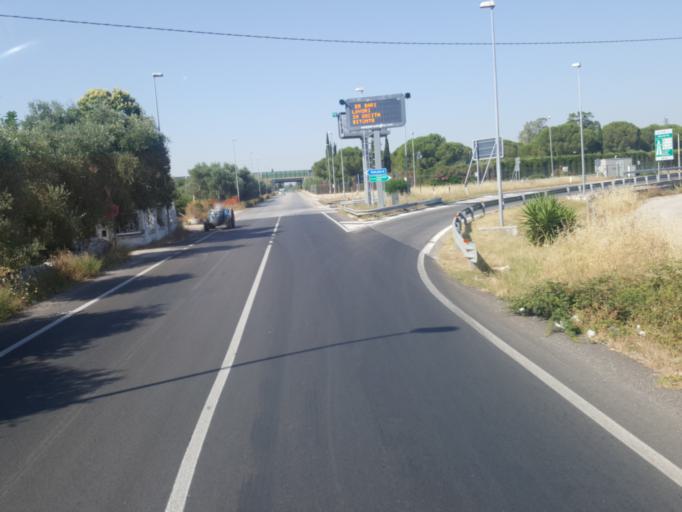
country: IT
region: Apulia
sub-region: Provincia di Bari
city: Molfetta
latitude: 41.1778
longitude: 16.5789
